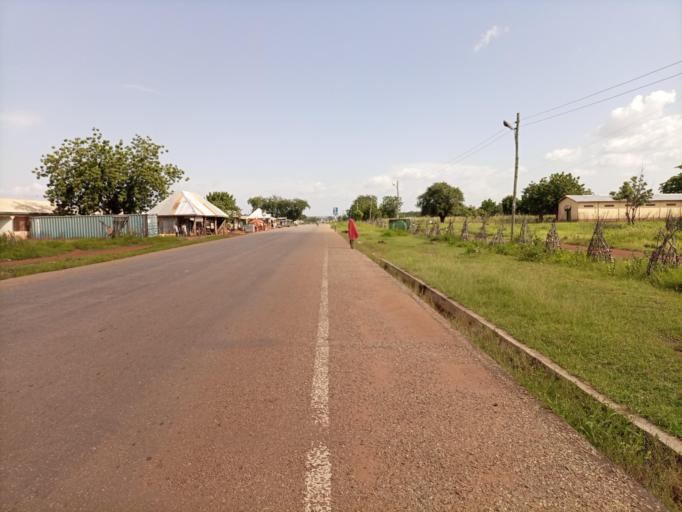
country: GH
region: Northern
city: Savelugu
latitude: 9.5524
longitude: -0.9434
